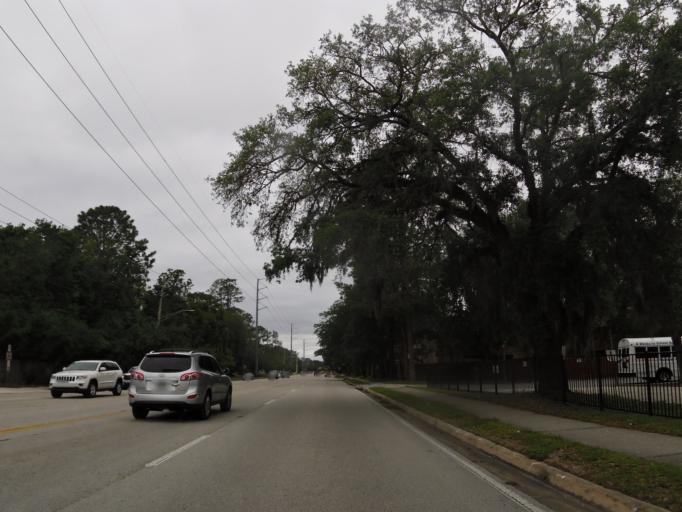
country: US
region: Florida
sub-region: Saint Johns County
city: Fruit Cove
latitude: 30.1788
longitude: -81.6055
